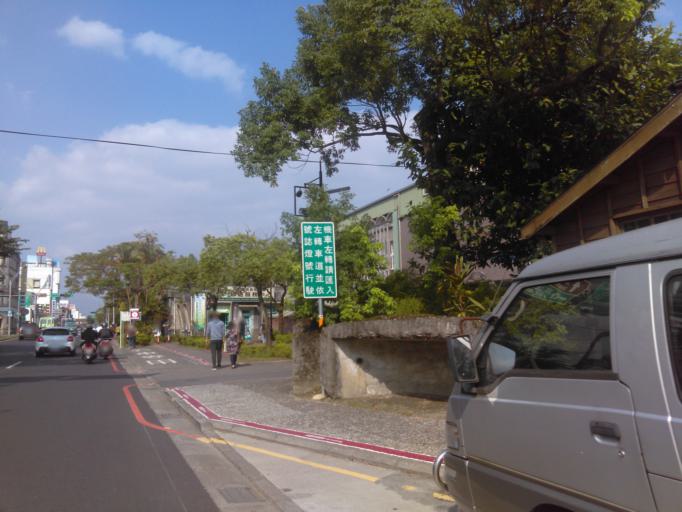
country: TW
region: Taiwan
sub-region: Yilan
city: Yilan
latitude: 24.7537
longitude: 121.7572
